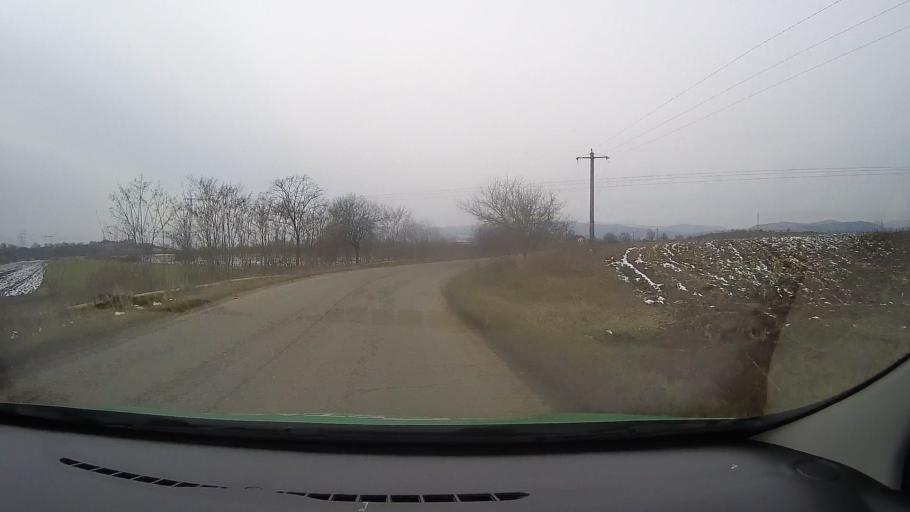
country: RO
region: Hunedoara
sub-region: Comuna Romos
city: Romos
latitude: 45.8750
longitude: 23.2659
